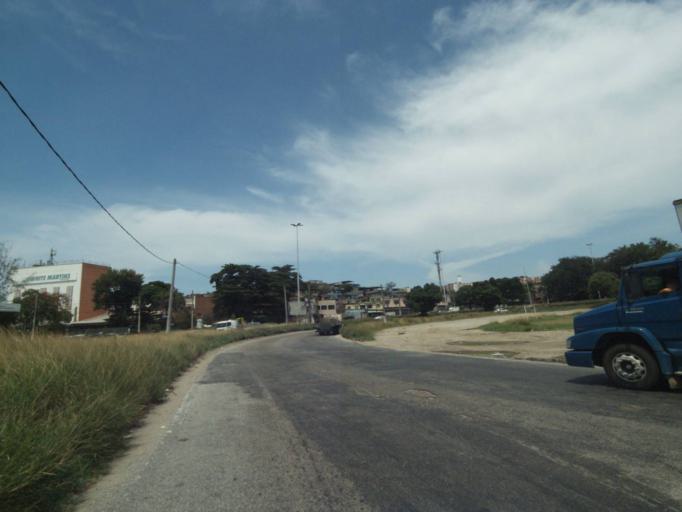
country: BR
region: Rio de Janeiro
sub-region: Duque De Caxias
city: Duque de Caxias
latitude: -22.8174
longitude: -43.2876
